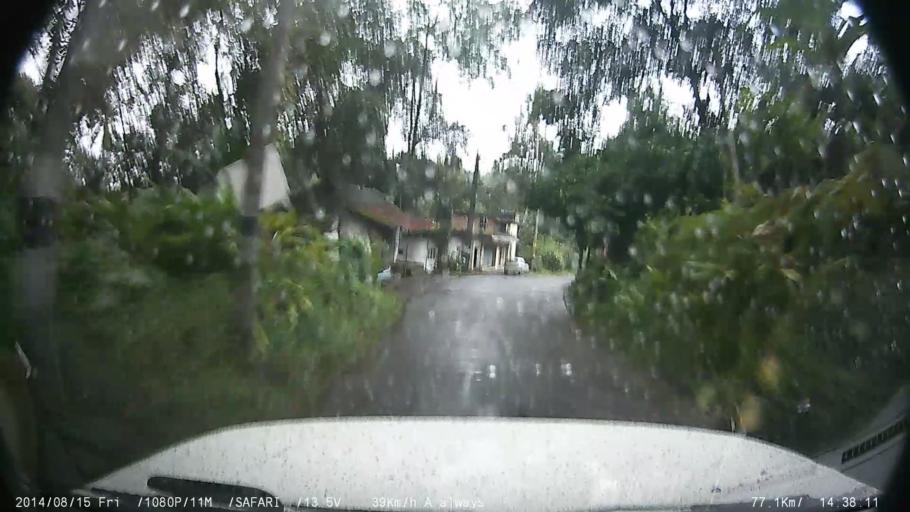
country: IN
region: Kerala
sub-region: Kottayam
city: Lalam
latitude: 9.8042
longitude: 76.7304
